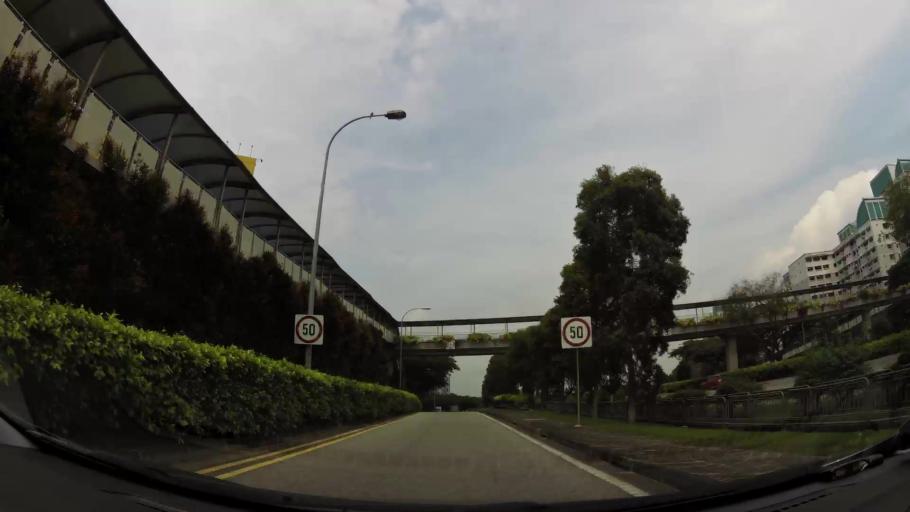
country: MY
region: Johor
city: Kampung Pasir Gudang Baru
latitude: 1.3745
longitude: 103.9342
